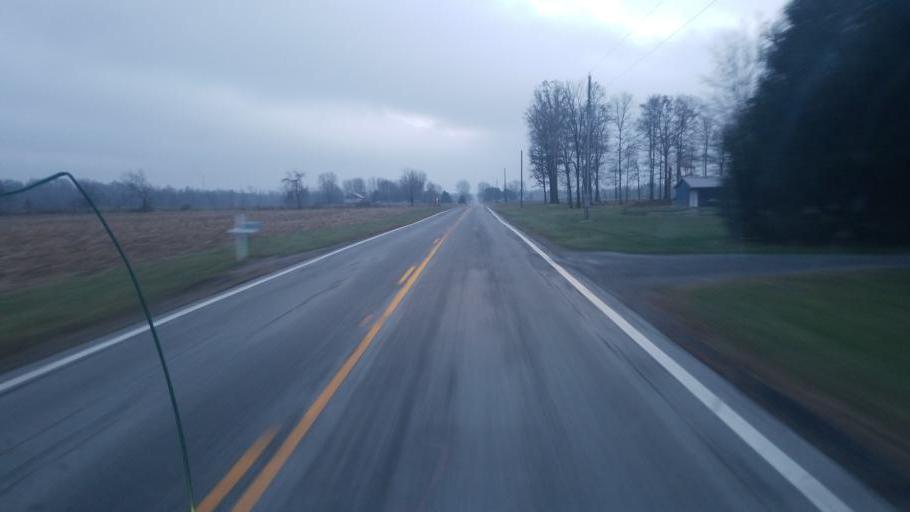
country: US
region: Ohio
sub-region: Wyandot County
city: Upper Sandusky
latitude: 40.8605
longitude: -83.1316
